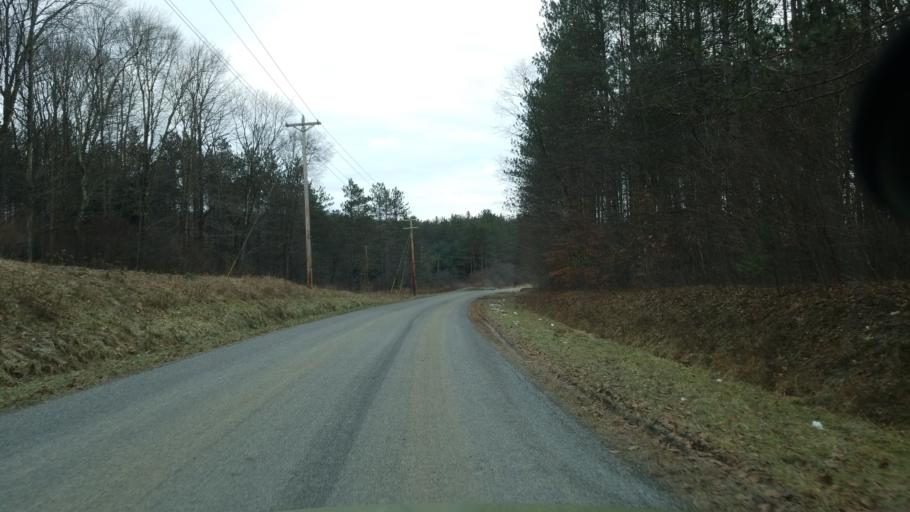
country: US
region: Pennsylvania
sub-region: Clearfield County
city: Treasure Lake
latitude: 41.1250
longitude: -78.6157
